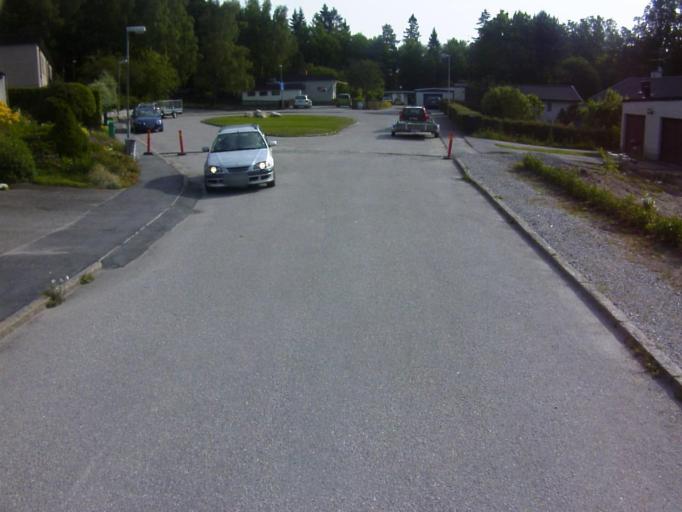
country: SE
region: Soedermanland
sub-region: Eskilstuna Kommun
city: Eskilstuna
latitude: 59.3538
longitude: 16.5201
